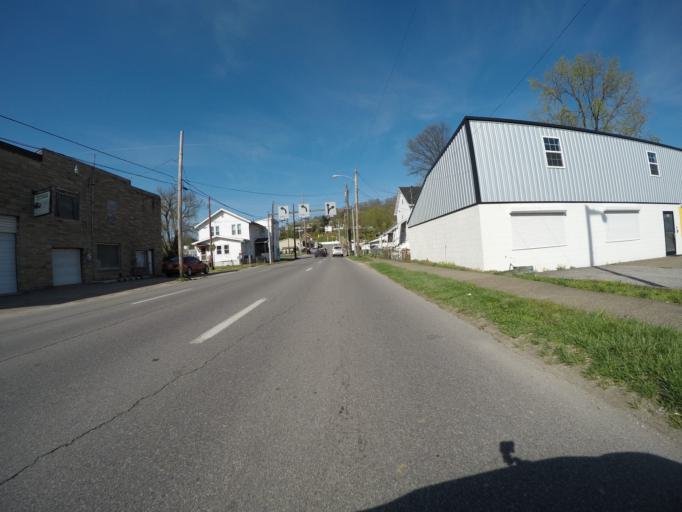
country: US
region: West Virginia
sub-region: Kanawha County
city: South Charleston
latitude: 38.3714
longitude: -81.6648
